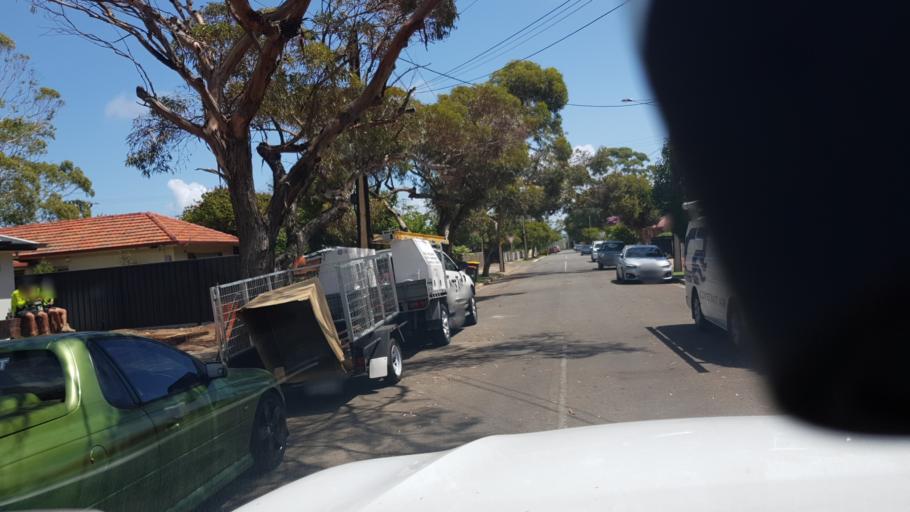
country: AU
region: South Australia
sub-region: Holdfast Bay
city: North Brighton
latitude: -34.9960
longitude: 138.5247
